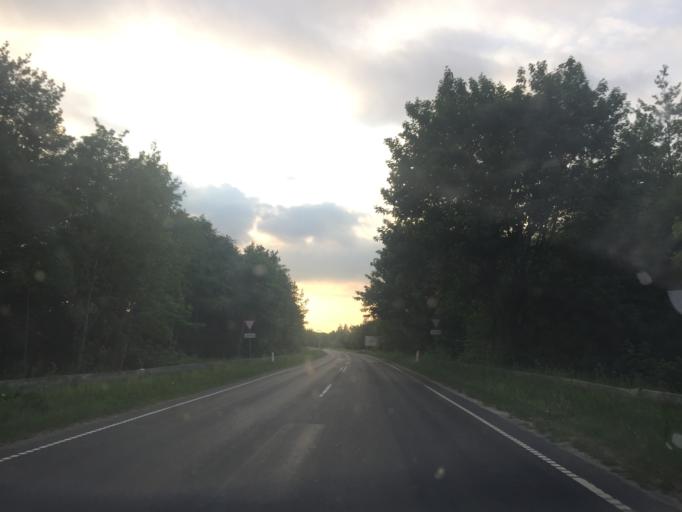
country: DK
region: South Denmark
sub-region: Odense Kommune
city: Neder Holluf
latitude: 55.3568
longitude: 10.4783
